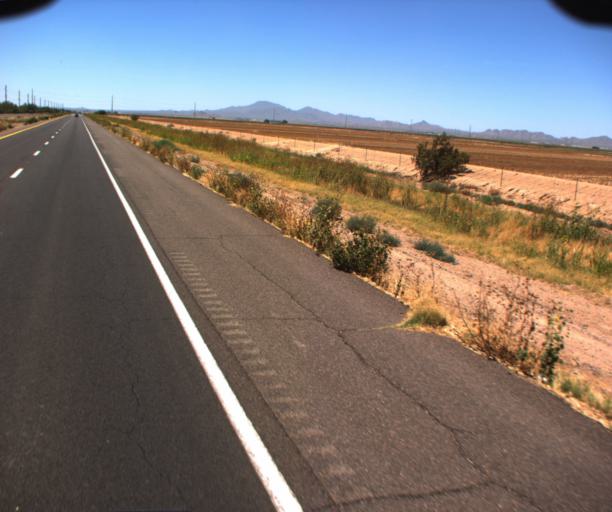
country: US
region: Arizona
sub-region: Pinal County
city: Maricopa
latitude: 32.9776
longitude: -112.0480
